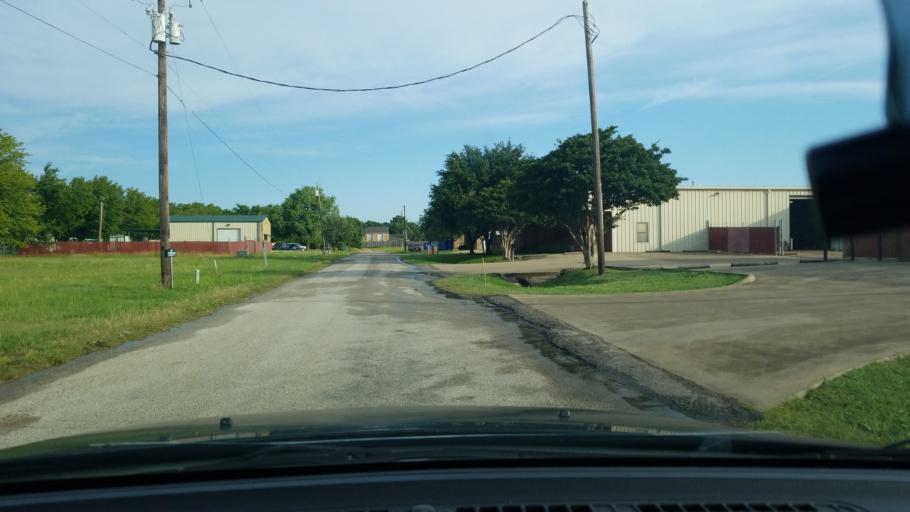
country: US
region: Texas
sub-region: Dallas County
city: Mesquite
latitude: 32.7966
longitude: -96.6196
